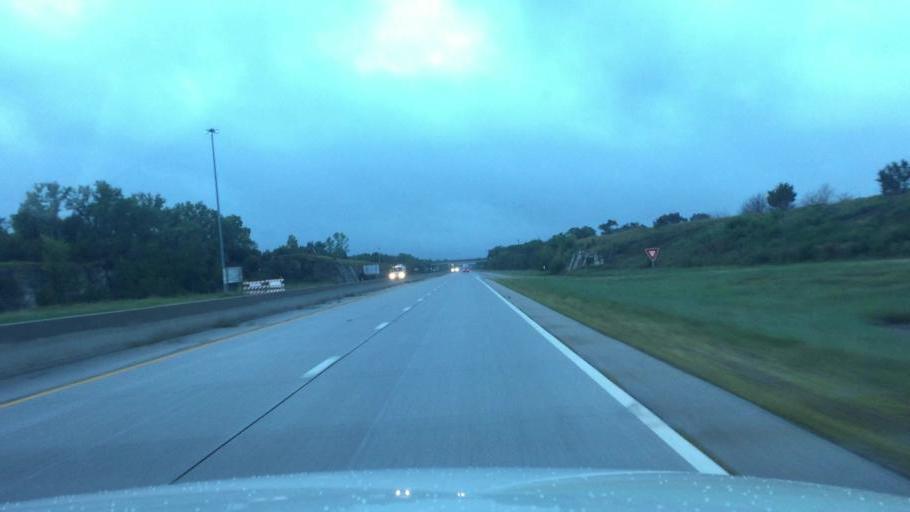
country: US
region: Kansas
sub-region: Neosho County
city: Chanute
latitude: 37.6876
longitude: -95.4796
